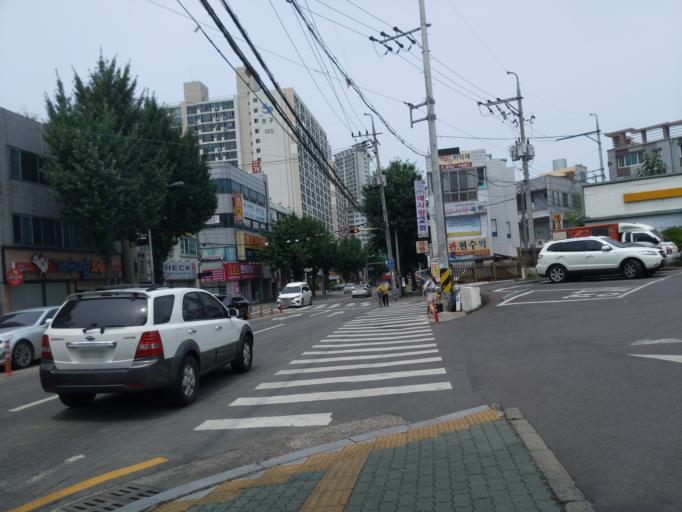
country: KR
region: Daegu
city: Hwawon
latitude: 35.8111
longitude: 128.5258
